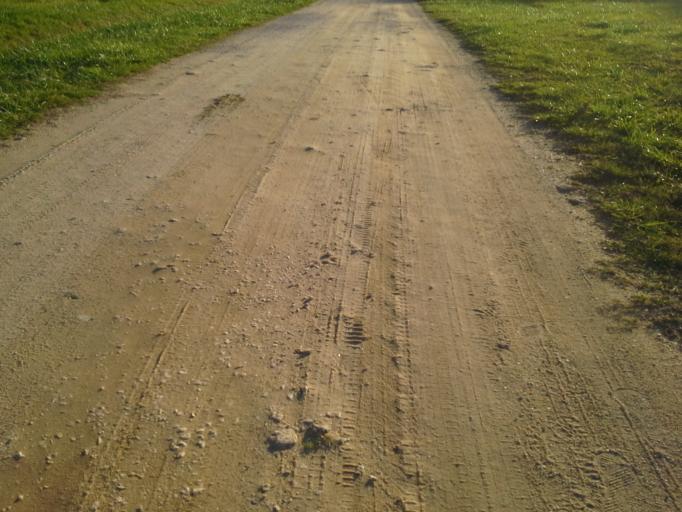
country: FR
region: Centre
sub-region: Departement du Loir-et-Cher
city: Saint-Romain-sur-Cher
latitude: 47.3662
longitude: 1.4016
